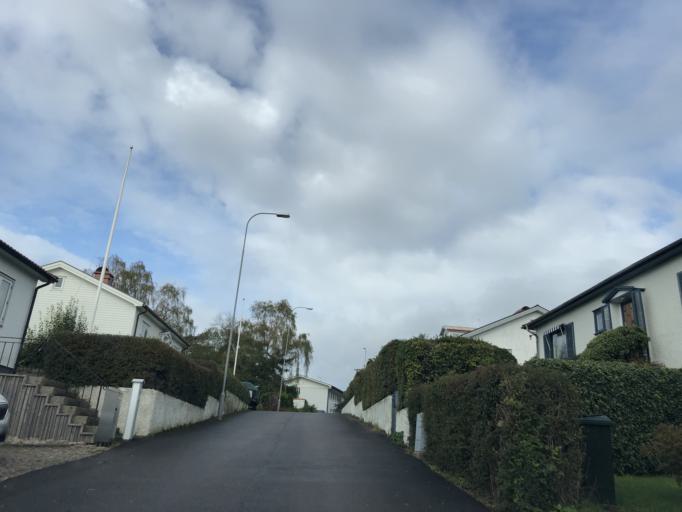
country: SE
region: Vaestra Goetaland
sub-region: Goteborg
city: Majorna
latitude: 57.6736
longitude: 11.8593
